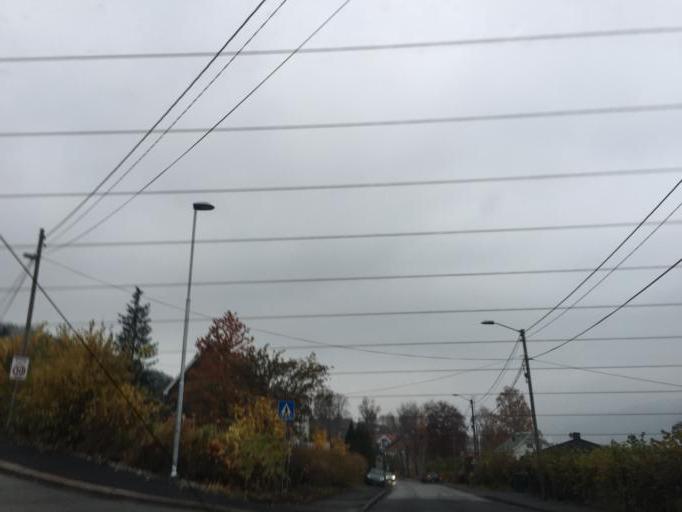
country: NO
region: Buskerud
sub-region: Drammen
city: Drammen
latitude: 59.7316
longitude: 10.1983
